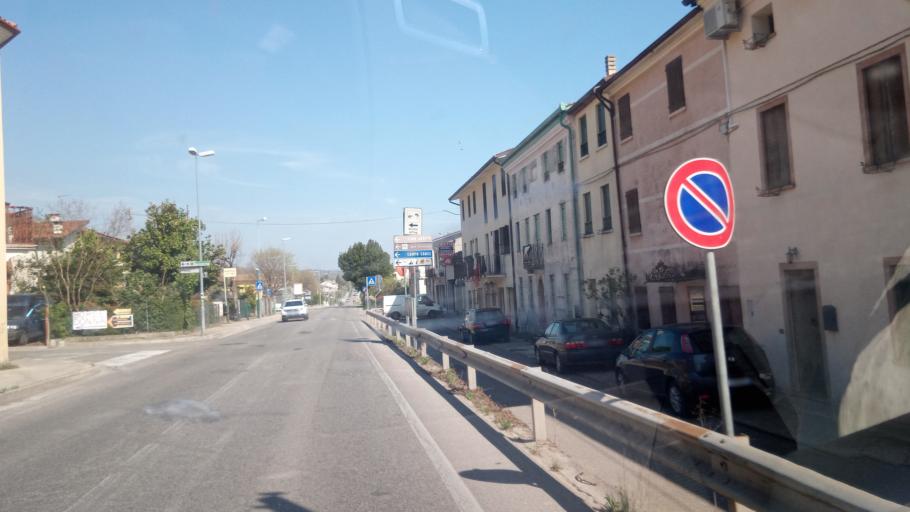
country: IT
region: Veneto
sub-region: Provincia di Treviso
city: Borso del Grappa
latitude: 45.8058
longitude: 11.7744
